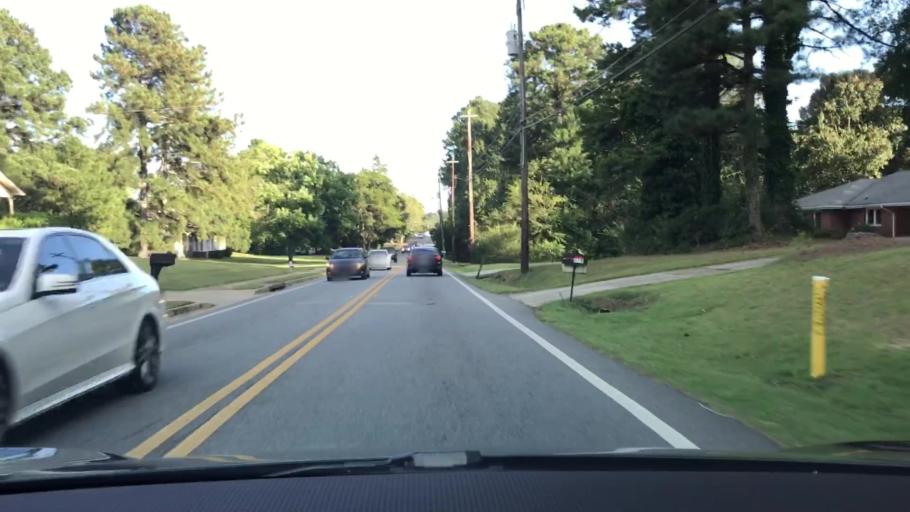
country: US
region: Georgia
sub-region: Gwinnett County
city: Dacula
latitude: 33.9967
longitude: -83.9027
